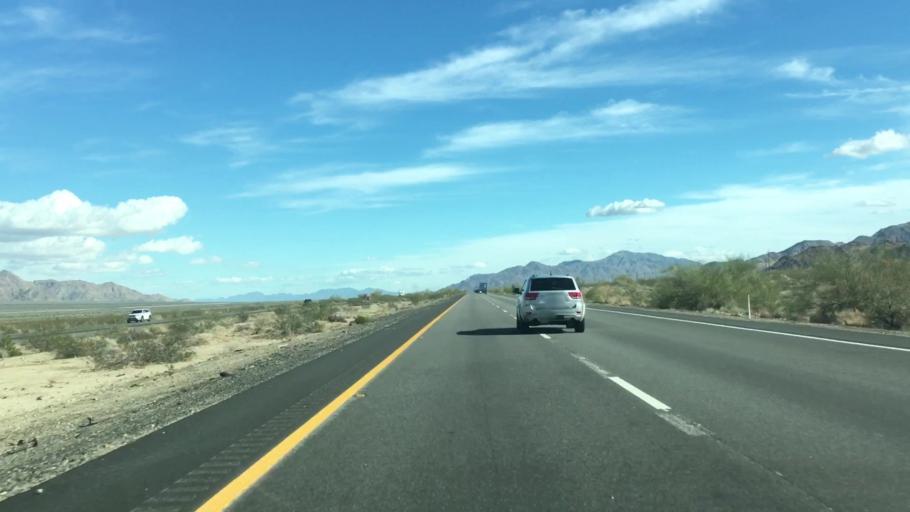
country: US
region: California
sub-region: Riverside County
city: Mecca
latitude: 33.6684
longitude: -115.6501
